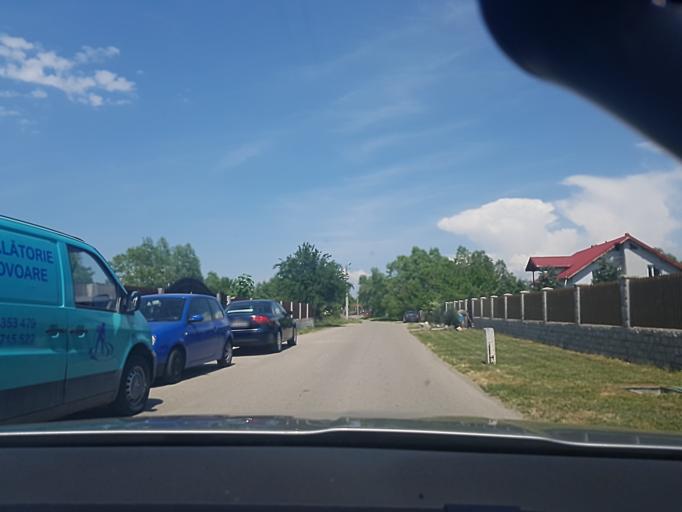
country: RO
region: Hunedoara
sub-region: Comuna Calan
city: Calan
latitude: 45.7377
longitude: 23.0089
